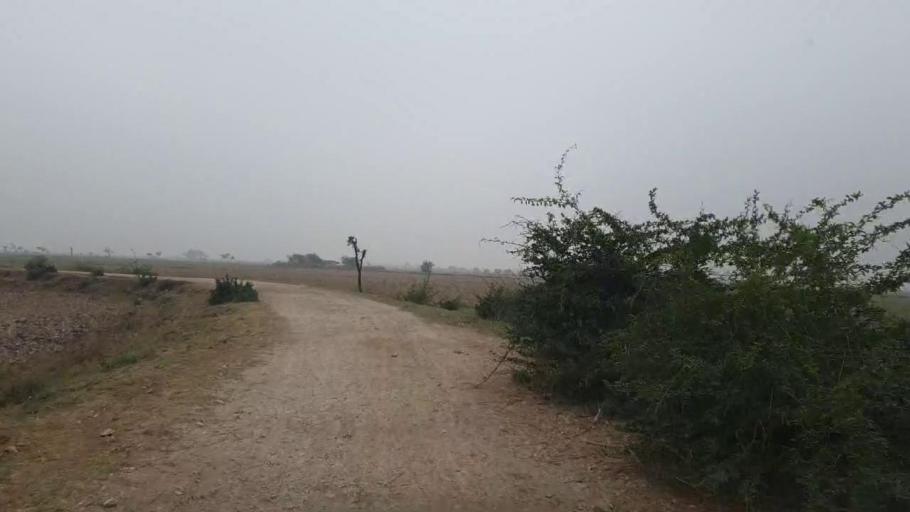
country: PK
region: Sindh
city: Badin
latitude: 24.6276
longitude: 68.6970
